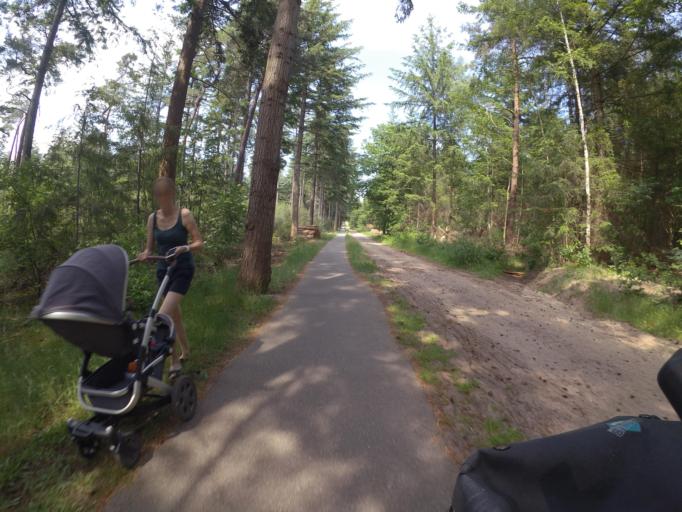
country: NL
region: Overijssel
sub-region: Gemeente Twenterand
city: Den Ham
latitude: 52.3737
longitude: 6.4318
